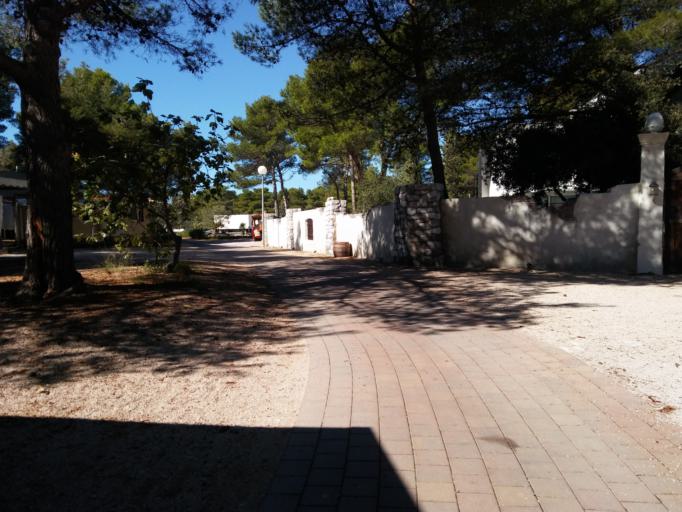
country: HR
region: Sibensko-Kniniska
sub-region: Grad Sibenik
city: Brodarica
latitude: 43.6967
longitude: 15.8901
